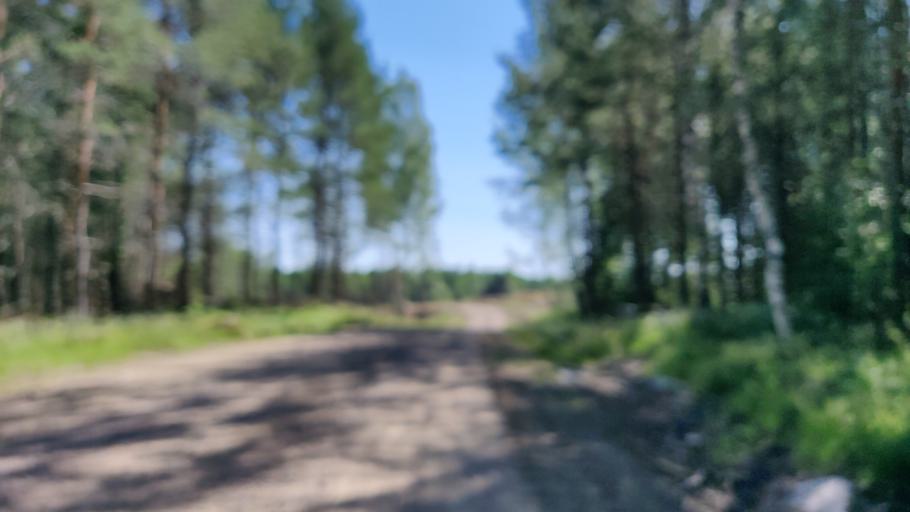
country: SE
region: Vaermland
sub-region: Hagfors Kommun
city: Hagfors
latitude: 59.9849
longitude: 13.5990
